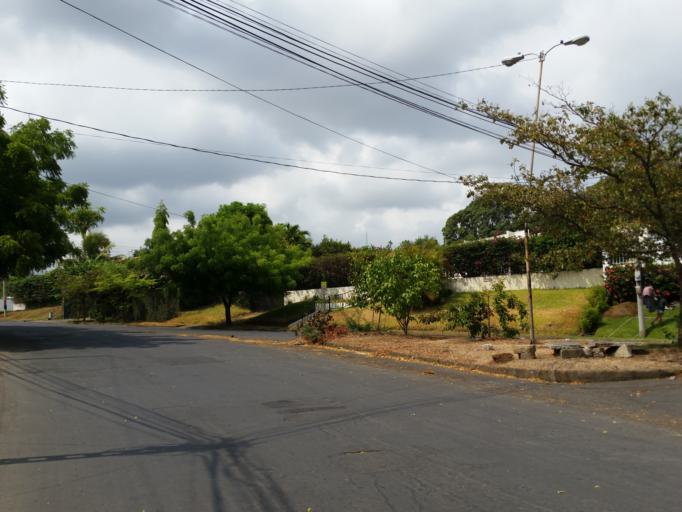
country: NI
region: Managua
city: Managua
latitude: 12.0833
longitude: -86.2454
